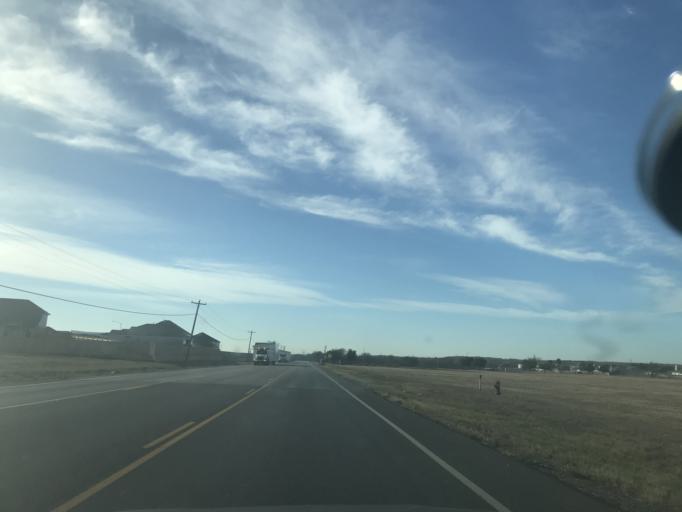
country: US
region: Texas
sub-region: Travis County
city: Manor
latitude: 30.3350
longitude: -97.5592
